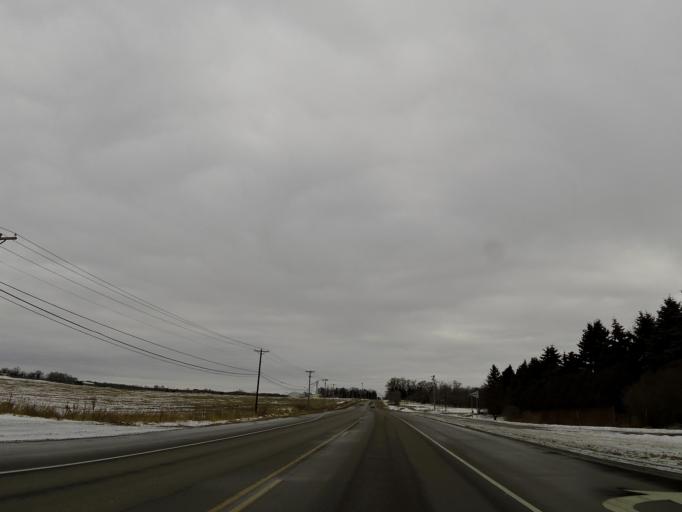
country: US
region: Minnesota
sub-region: Washington County
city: Cottage Grove
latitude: 44.8419
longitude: -92.9038
